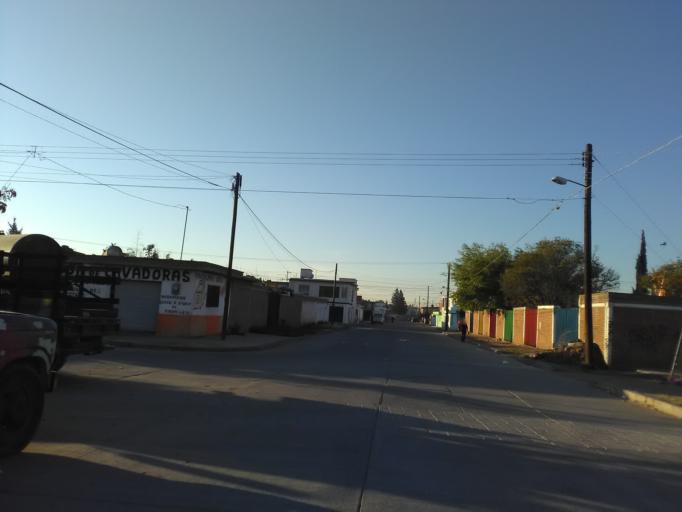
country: MX
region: Durango
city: Victoria de Durango
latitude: 24.0523
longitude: -104.6388
